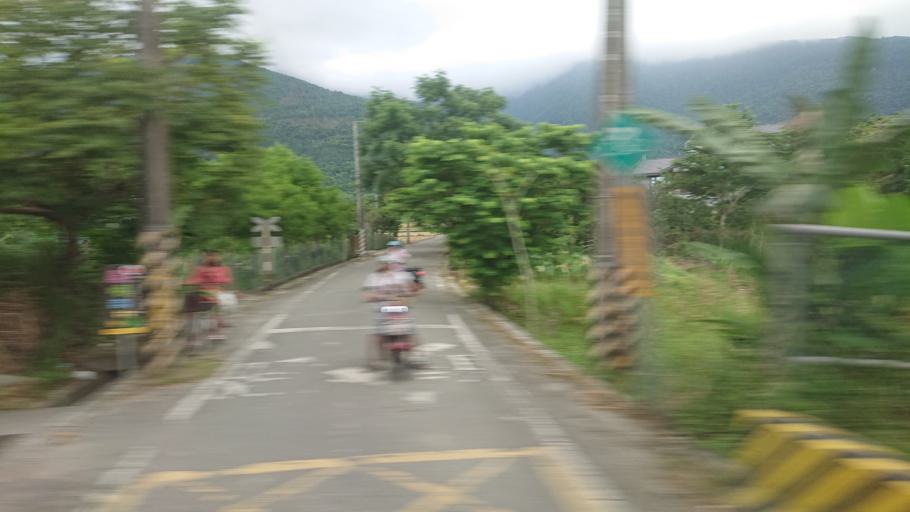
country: TW
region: Taiwan
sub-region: Hualien
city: Hualian
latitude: 23.7397
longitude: 121.4434
